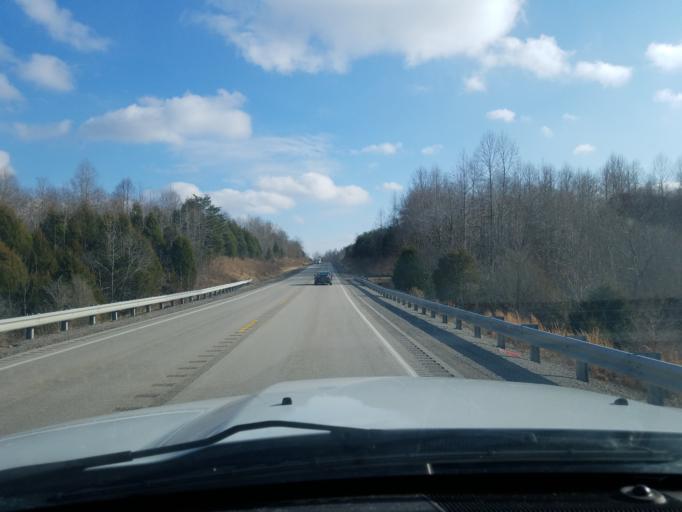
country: US
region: Kentucky
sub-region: Larue County
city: Hodgenville
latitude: 37.4738
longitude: -85.6080
